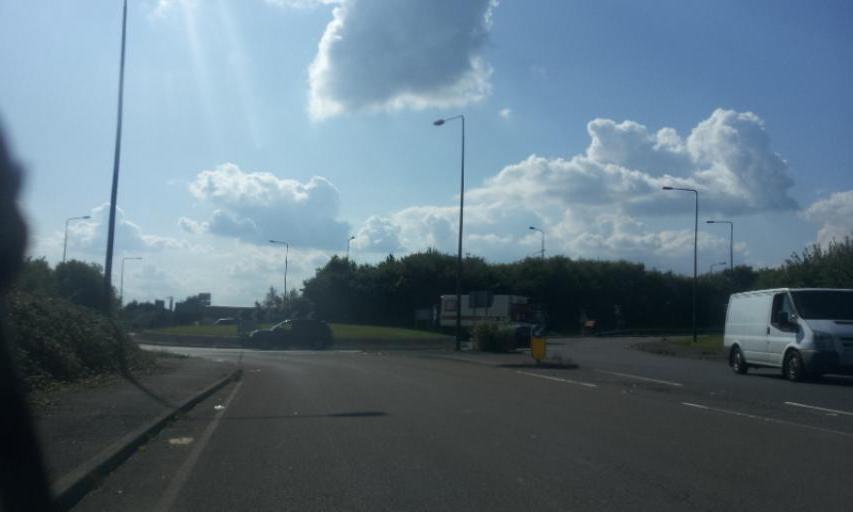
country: GB
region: England
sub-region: Kent
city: East Peckham
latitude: 51.2248
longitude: 0.3977
